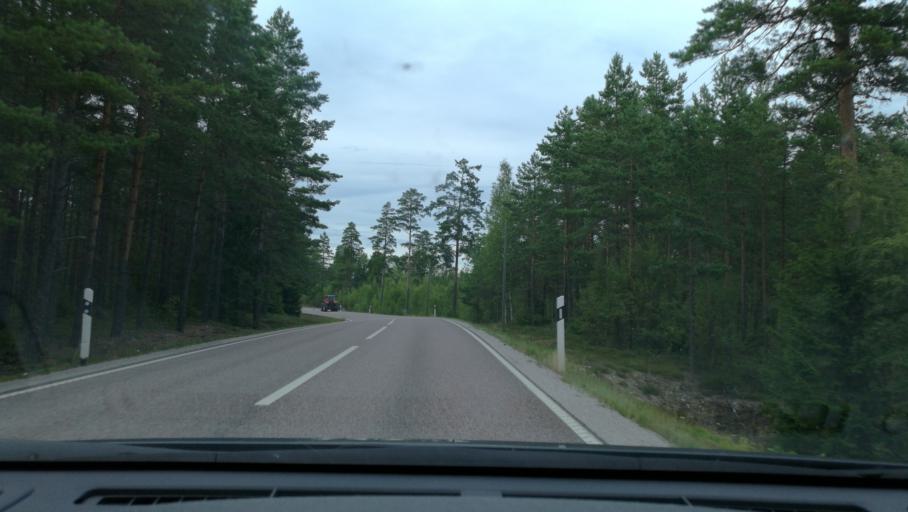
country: SE
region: Vaestmanland
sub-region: Kungsors Kommun
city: Kungsoer
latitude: 59.3285
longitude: 16.1118
